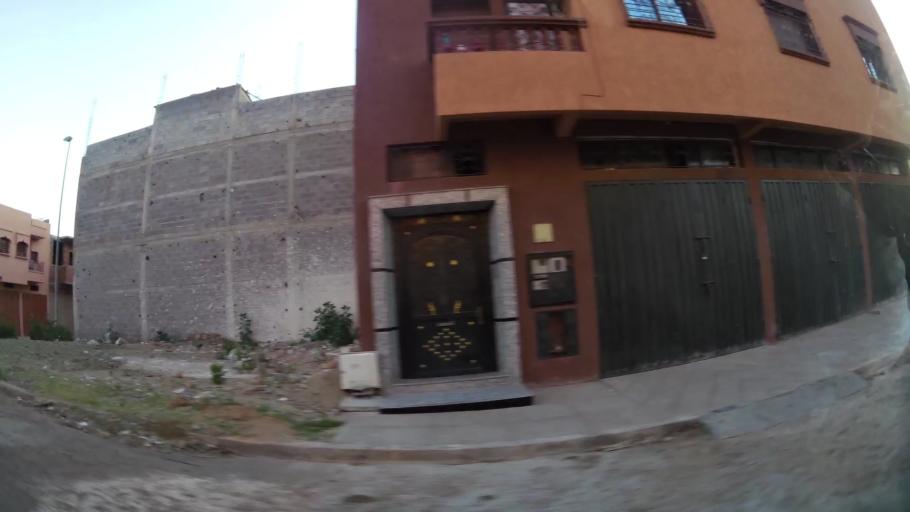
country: MA
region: Marrakech-Tensift-Al Haouz
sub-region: Kelaa-Des-Sraghna
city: Sidi Abdallah
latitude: 32.2388
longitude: -7.9414
